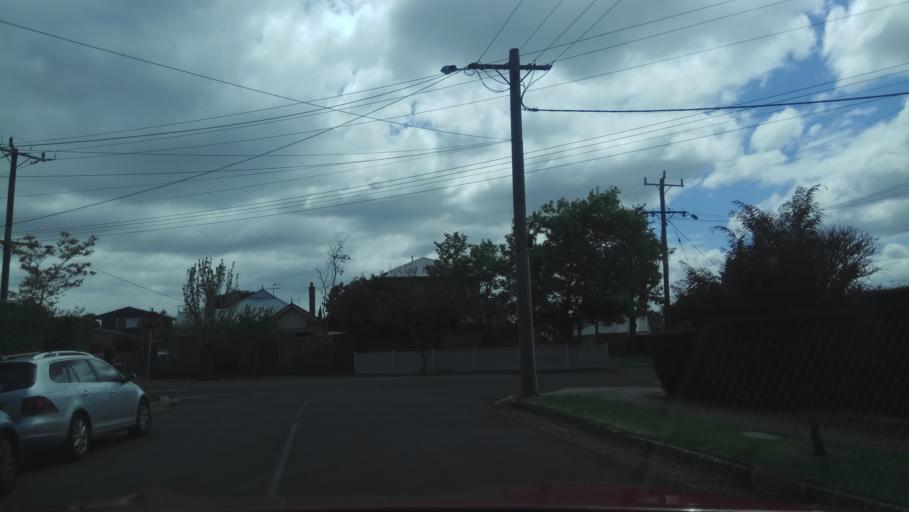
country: AU
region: Victoria
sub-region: Hobsons Bay
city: Newport
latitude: -37.8507
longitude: 144.8900
